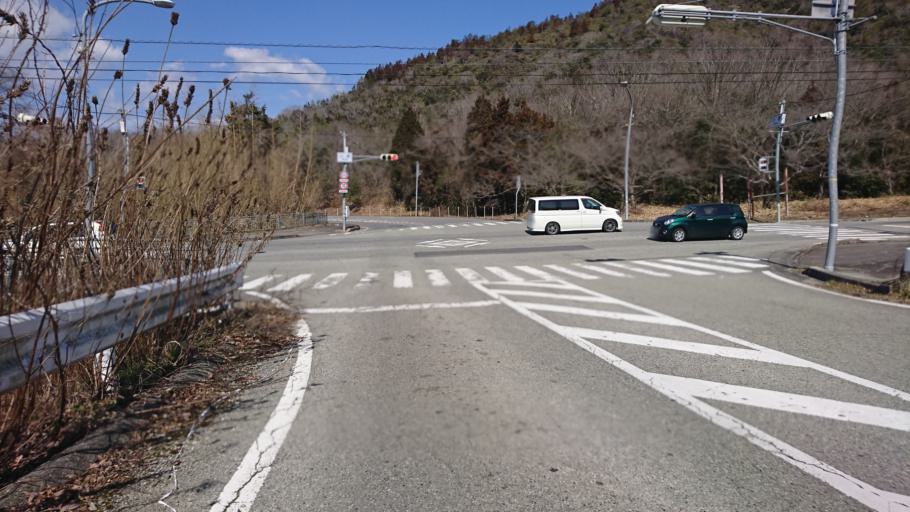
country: JP
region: Hyogo
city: Kakogawacho-honmachi
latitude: 34.8666
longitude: 134.7971
